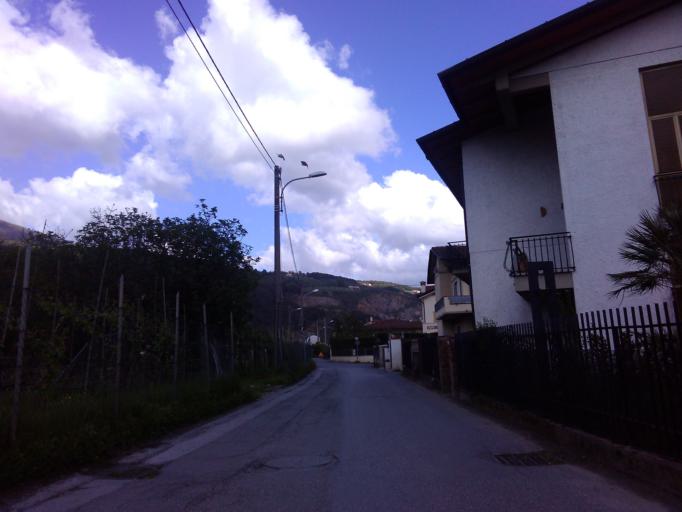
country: IT
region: Tuscany
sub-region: Provincia di Massa-Carrara
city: Capanne-Prato-Cinquale
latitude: 44.0003
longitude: 10.1610
